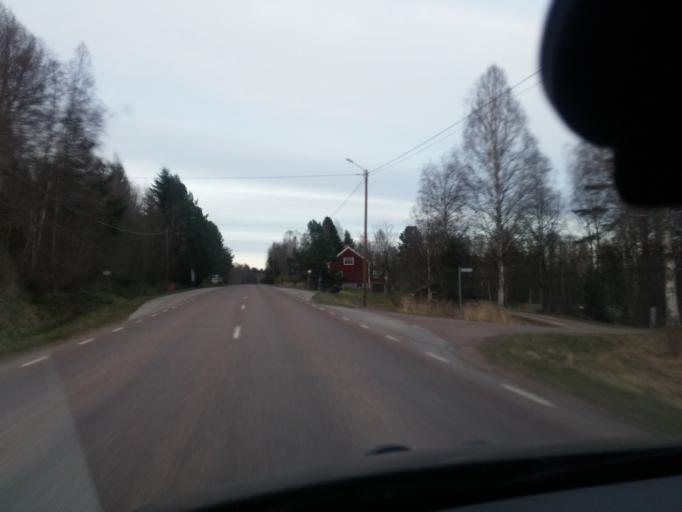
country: SE
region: Dalarna
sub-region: Faluns Kommun
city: Bjursas
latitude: 60.7154
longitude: 15.3236
